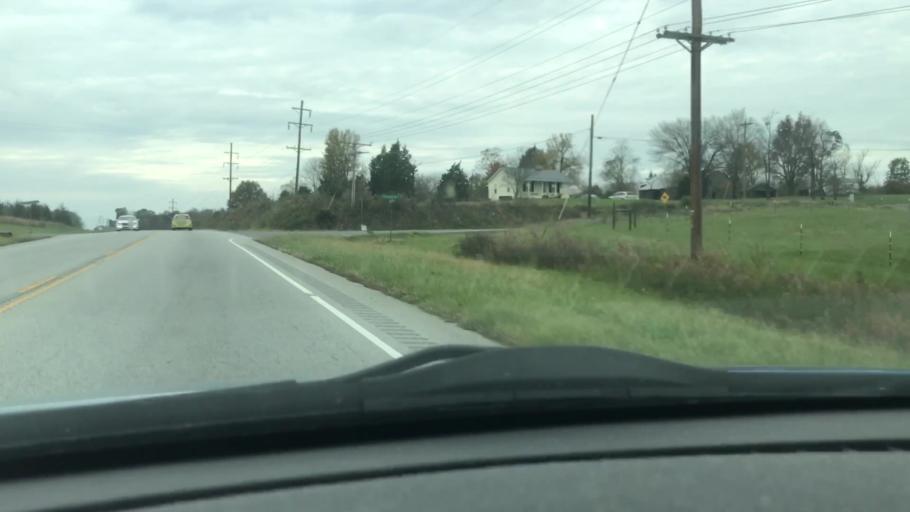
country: US
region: North Carolina
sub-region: Randolph County
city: Trinity
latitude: 35.7514
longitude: -80.0163
